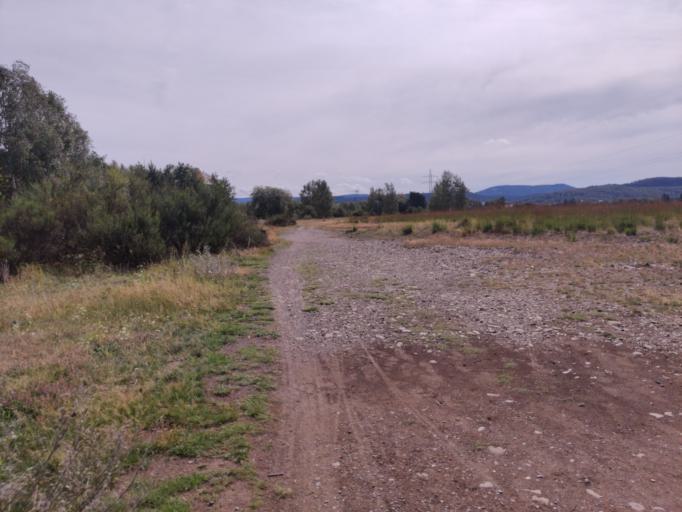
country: DE
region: Lower Saxony
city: Langelsheim
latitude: 51.9503
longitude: 10.3484
